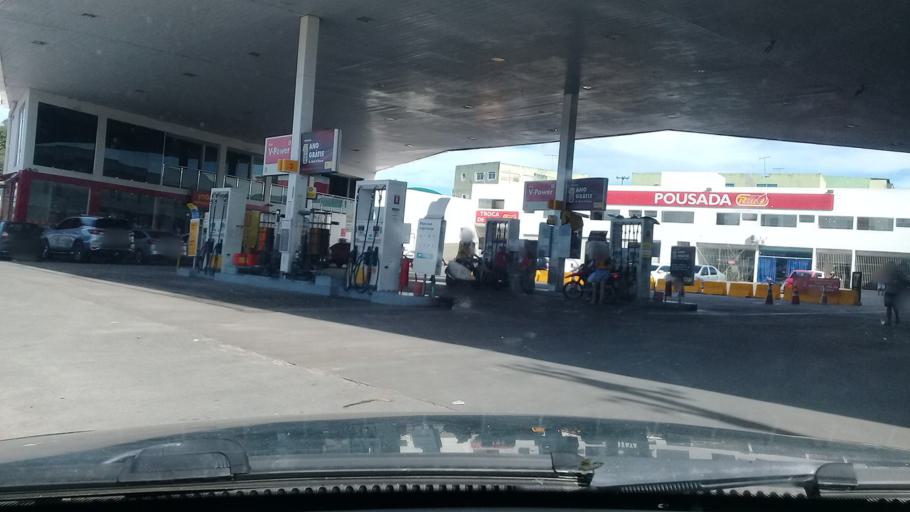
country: BR
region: Pernambuco
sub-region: Vitoria De Santo Antao
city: Vitoria de Santo Antao
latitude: -8.1123
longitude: -35.2896
